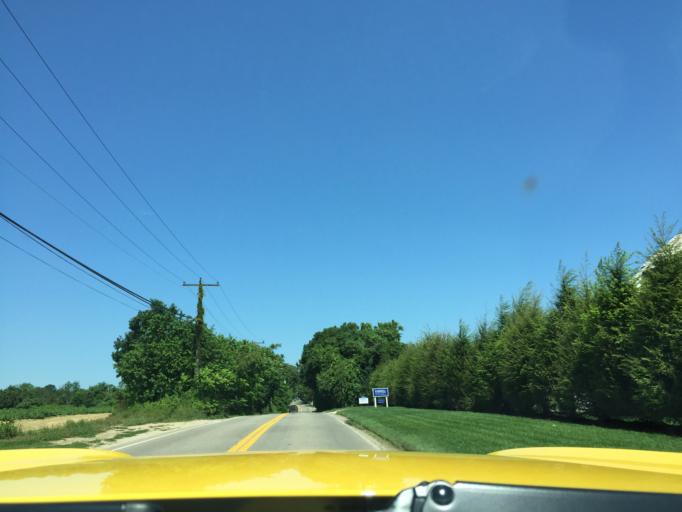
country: US
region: New York
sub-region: Suffolk County
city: Bridgehampton
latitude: 40.9404
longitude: -72.2592
